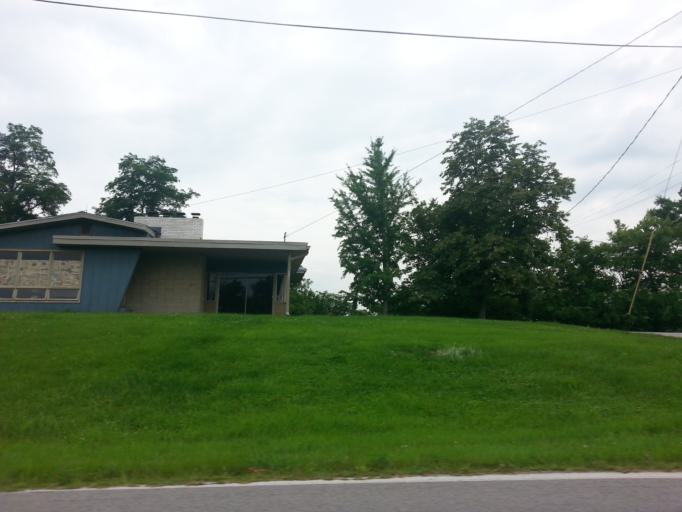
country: US
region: Kentucky
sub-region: Robertson County
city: Mount Olivet
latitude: 38.5346
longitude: -84.0315
